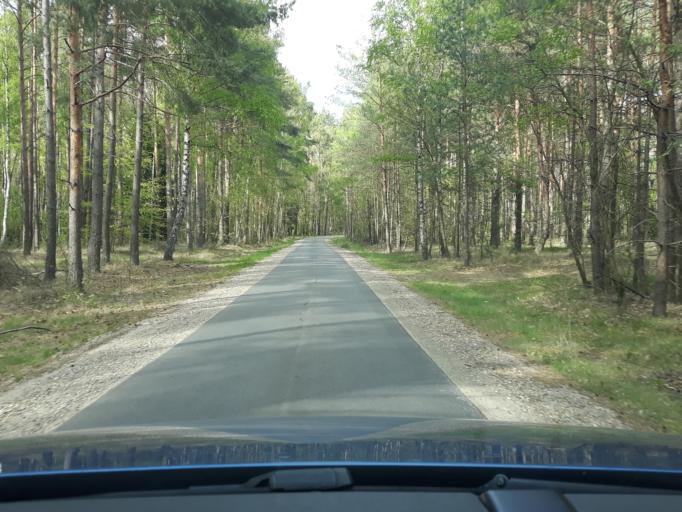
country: PL
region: Pomeranian Voivodeship
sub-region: Powiat czluchowski
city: Czluchow
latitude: 53.7231
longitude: 17.3345
